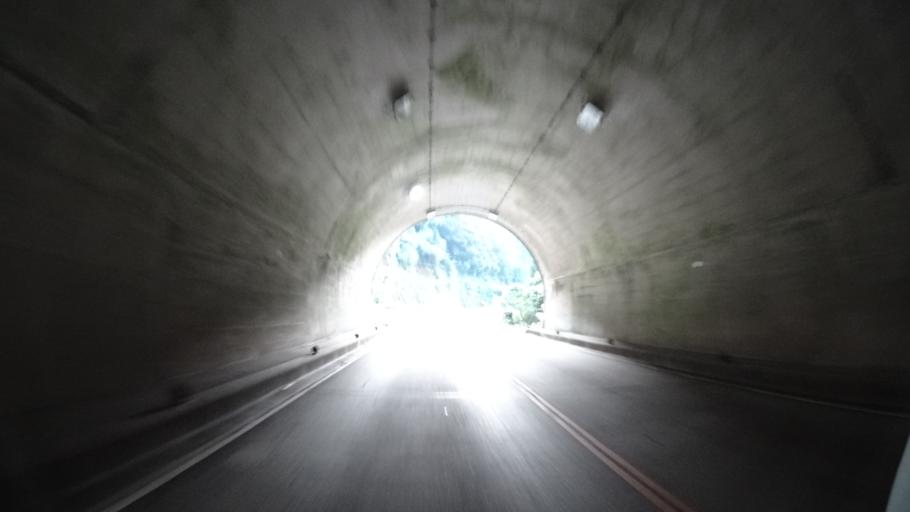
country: JP
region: Kumamoto
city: Minamata
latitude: 32.1600
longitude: 130.5083
